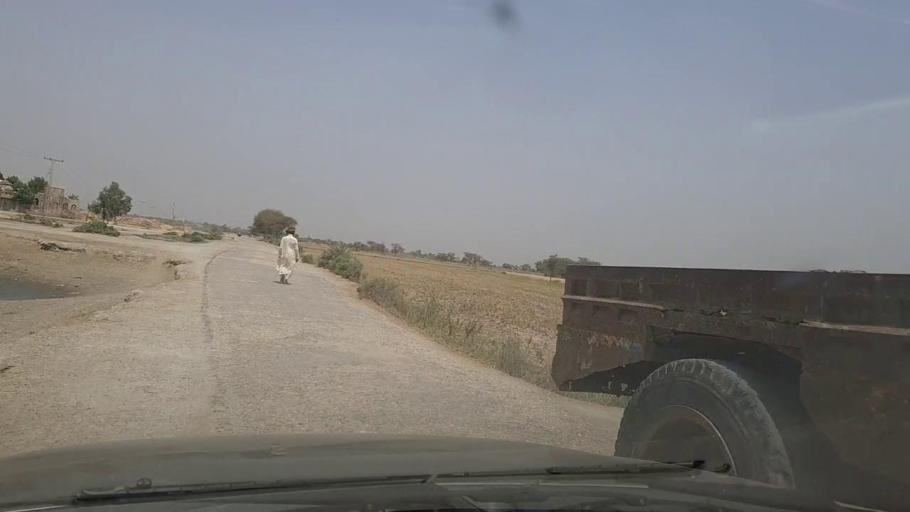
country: PK
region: Balochistan
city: Sohbatpur
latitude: 28.4176
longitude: 68.6847
